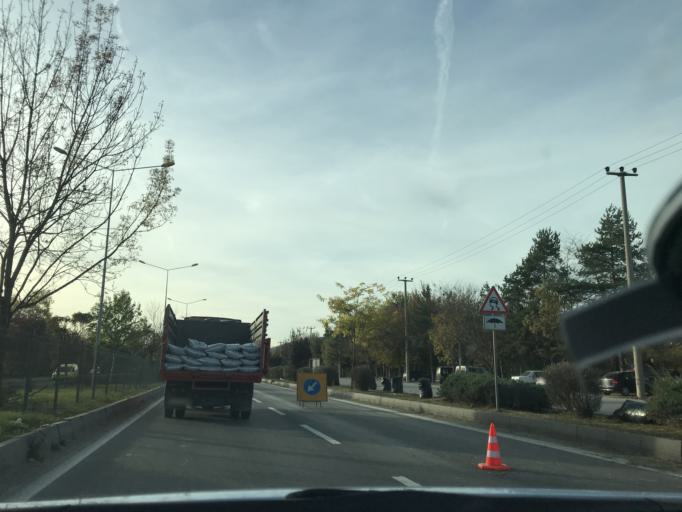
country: TR
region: Bolu
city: Bolu
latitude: 40.7377
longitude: 31.6179
